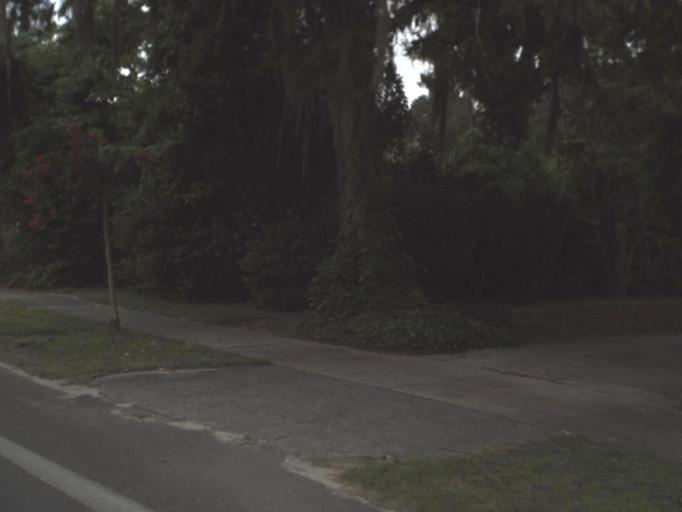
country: US
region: Florida
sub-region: Hamilton County
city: Jasper
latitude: 30.5155
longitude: -82.9460
